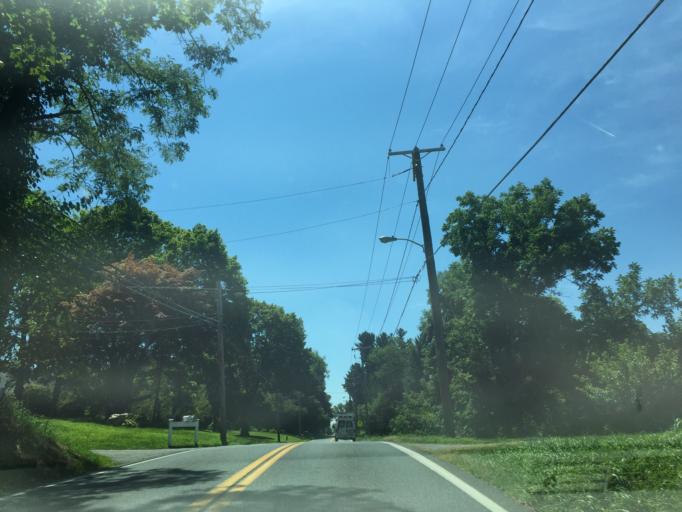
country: US
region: Maryland
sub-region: Harford County
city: Bel Air North
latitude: 39.5908
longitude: -76.3879
